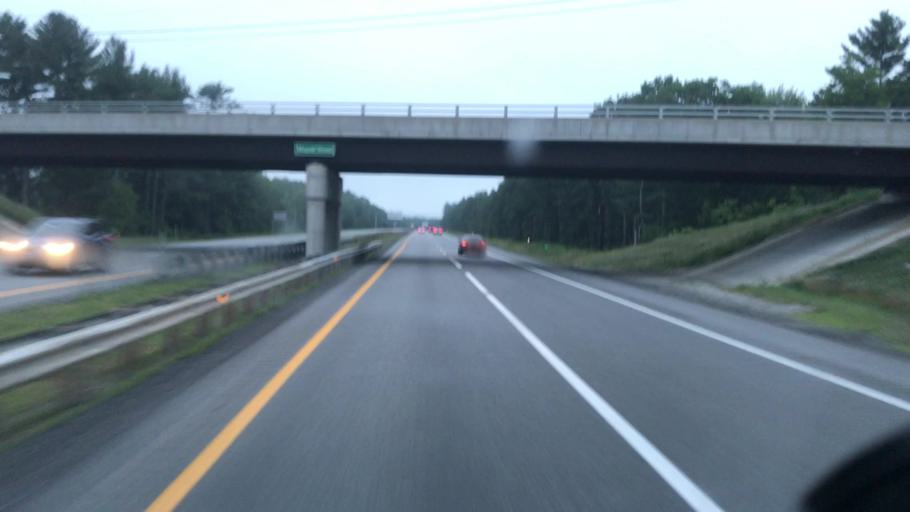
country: US
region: Maine
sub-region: Cumberland County
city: New Gloucester
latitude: 43.9415
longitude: -70.3338
